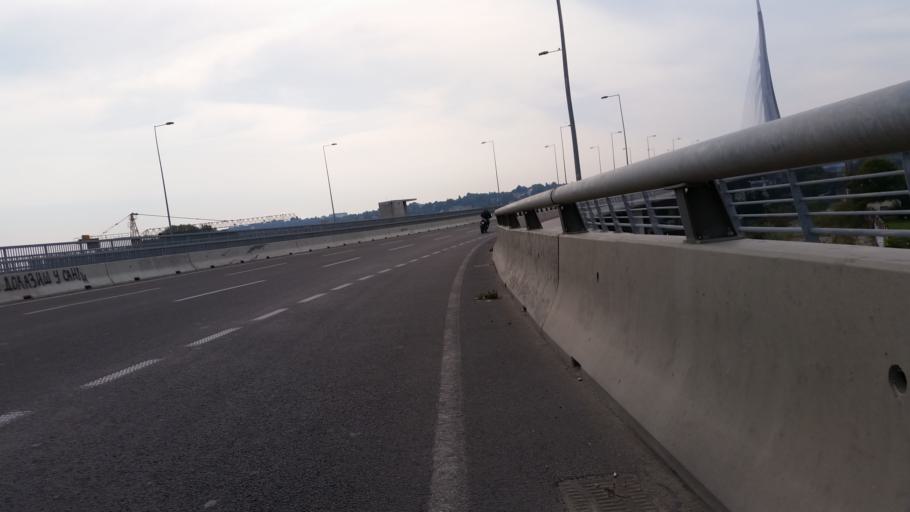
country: RS
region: Central Serbia
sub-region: Belgrade
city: Novi Beograd
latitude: 44.8024
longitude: 20.4241
